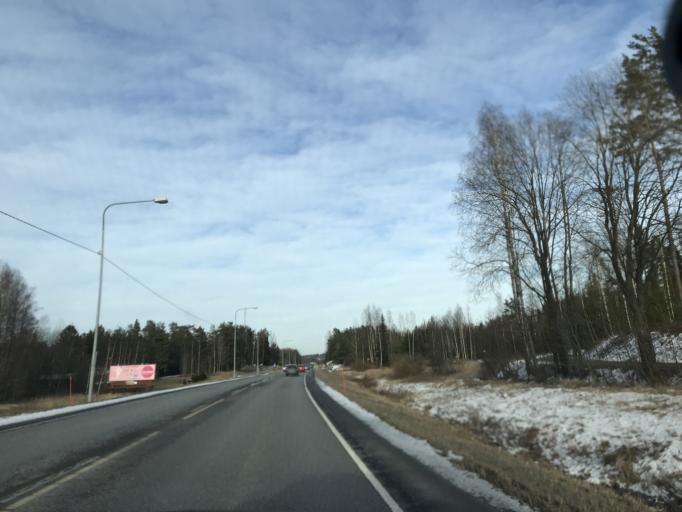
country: FI
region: Uusimaa
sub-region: Helsinki
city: Kirkkonummi
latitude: 60.1092
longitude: 24.3797
